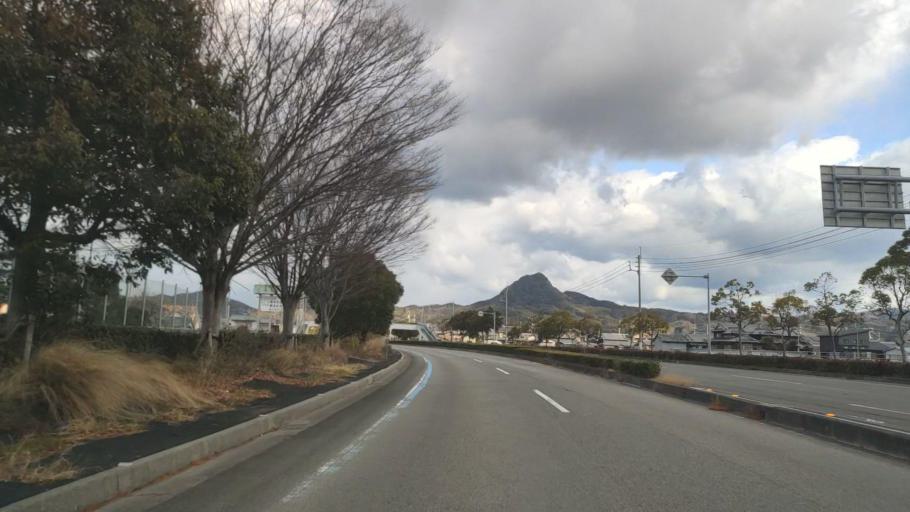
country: JP
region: Ehime
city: Hojo
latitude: 33.9700
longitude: 132.7833
